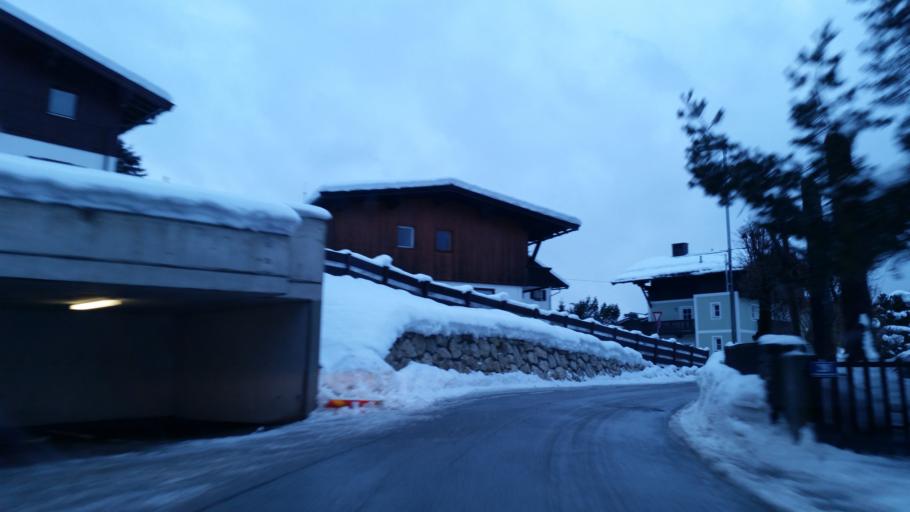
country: AT
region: Tyrol
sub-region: Politischer Bezirk Kitzbuhel
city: Sankt Johann in Tirol
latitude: 47.5188
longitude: 12.4261
